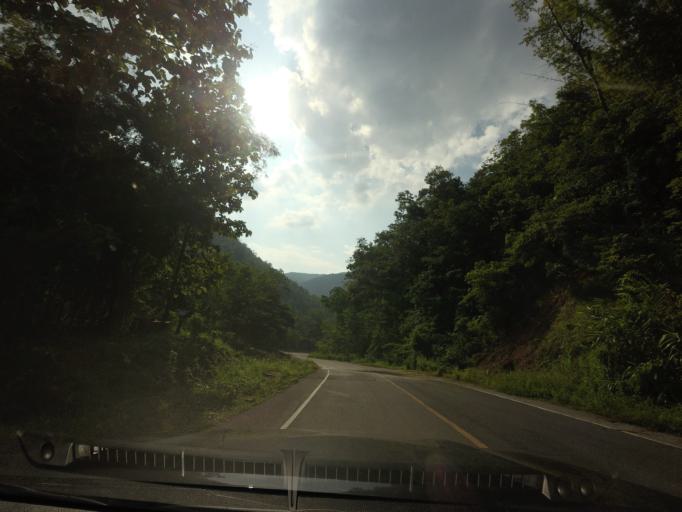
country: TH
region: Nan
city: Na Noi
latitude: 18.3133
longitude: 100.8969
